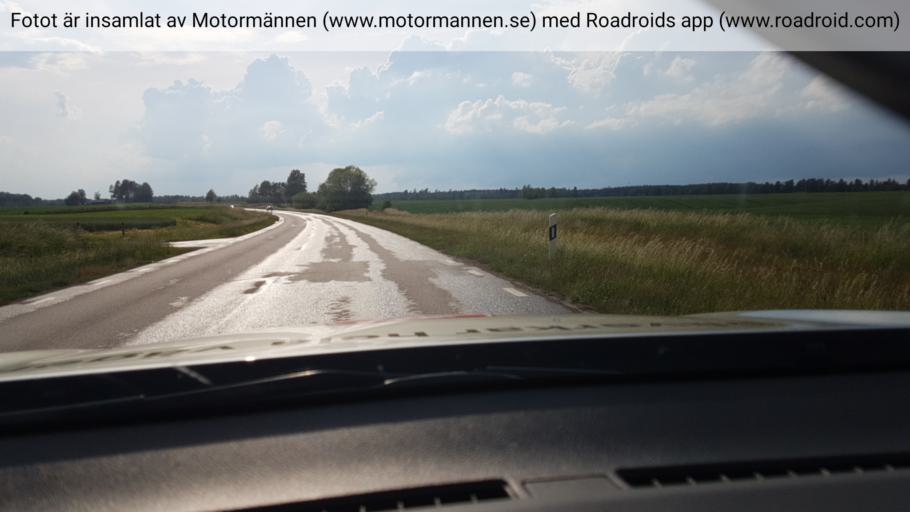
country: SE
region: Vaestra Goetaland
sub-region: Tibro Kommun
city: Tibro
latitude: 58.3470
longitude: 14.1402
